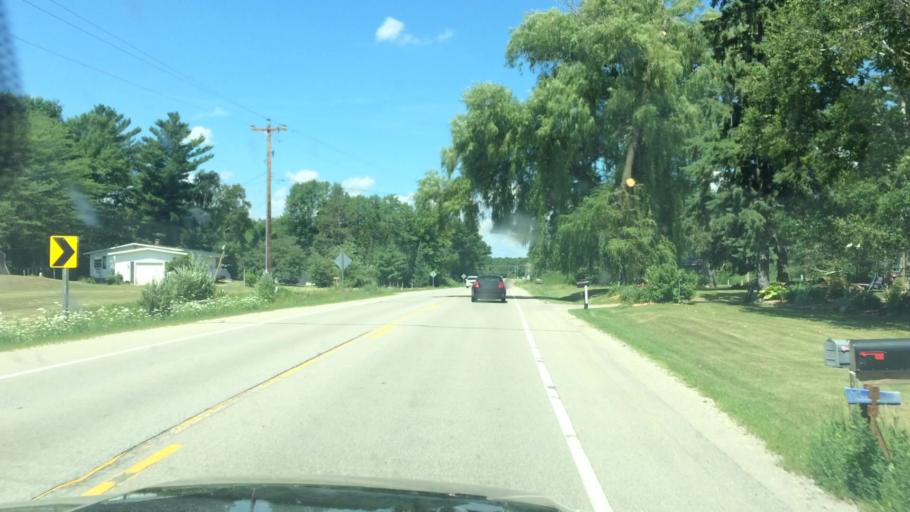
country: US
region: Wisconsin
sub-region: Marinette County
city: Peshtigo
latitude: 45.1014
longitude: -87.7451
